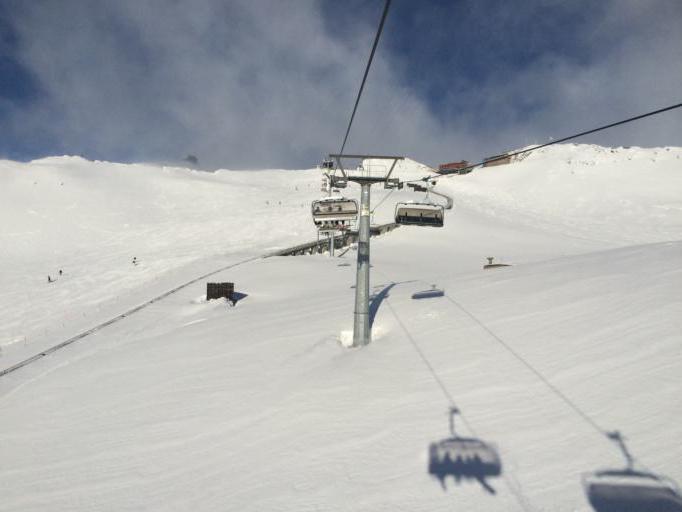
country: CH
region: Grisons
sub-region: Praettigau/Davos District
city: Davos
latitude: 46.8285
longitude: 9.8098
